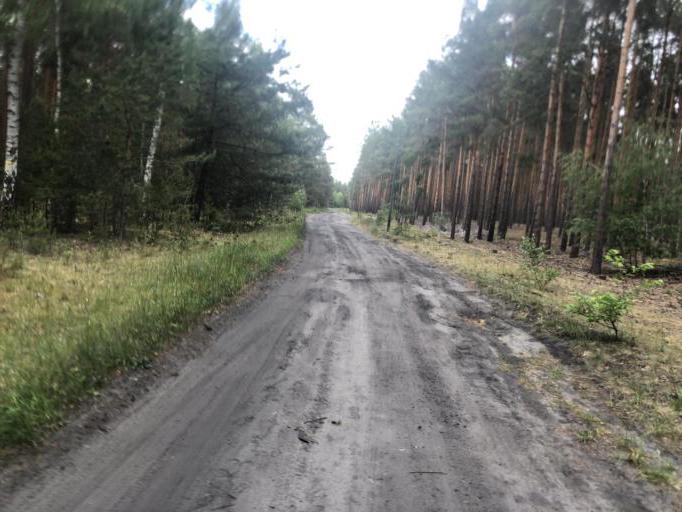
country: DE
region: Brandenburg
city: Gross Koris
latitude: 52.1873
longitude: 13.6499
